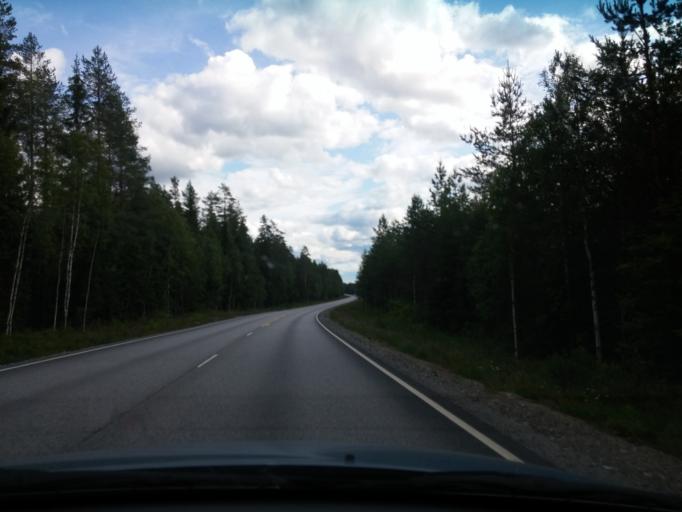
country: FI
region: Central Finland
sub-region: Keuruu
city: Multia
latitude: 62.5366
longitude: 24.6312
